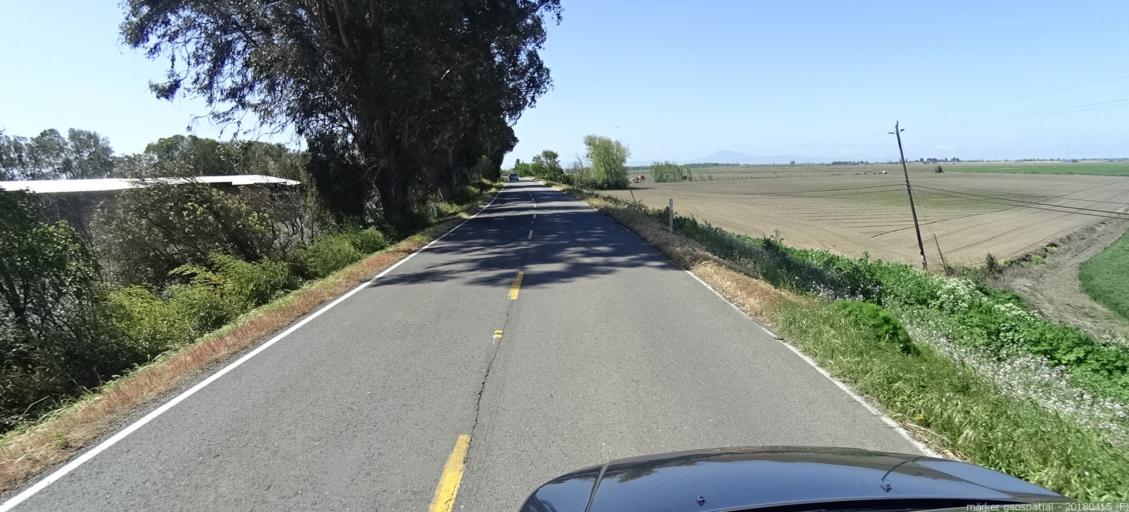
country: US
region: California
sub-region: Solano County
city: Rio Vista
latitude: 38.1248
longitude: -121.5841
